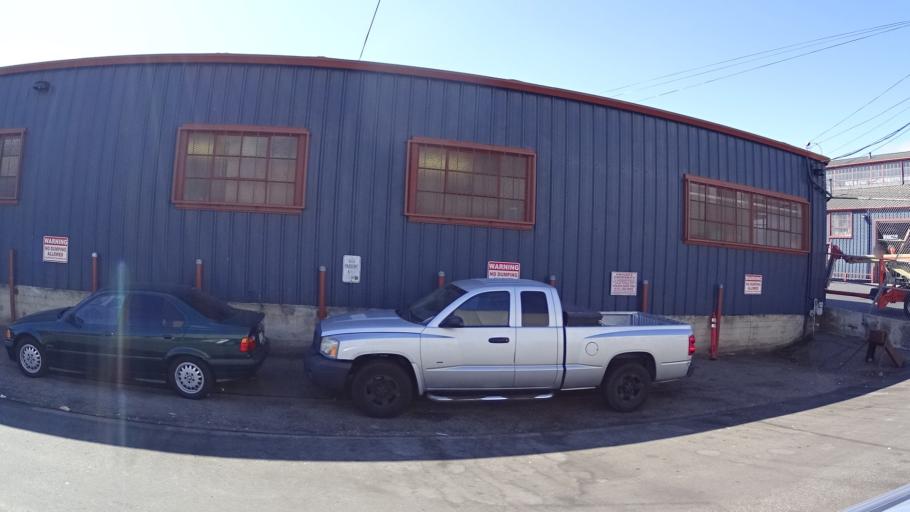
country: US
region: California
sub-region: San Mateo County
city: Brisbane
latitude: 37.7271
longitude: -122.4005
